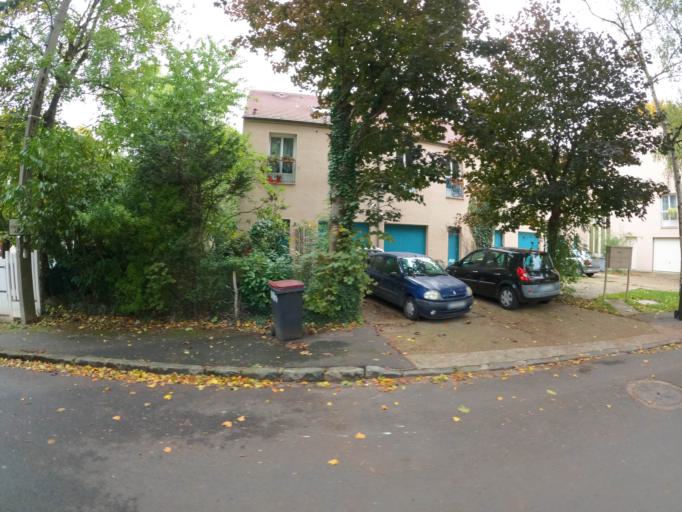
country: FR
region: Ile-de-France
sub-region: Departement du Val-de-Marne
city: Sucy-en-Brie
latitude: 48.7765
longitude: 2.5198
